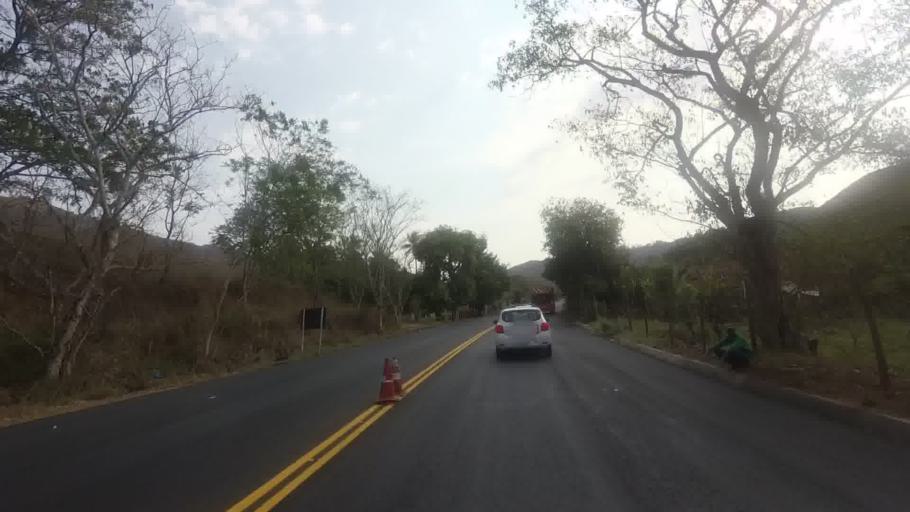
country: BR
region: Rio de Janeiro
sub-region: Bom Jesus Do Itabapoana
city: Bom Jesus do Itabapoana
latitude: -21.2110
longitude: -41.7280
